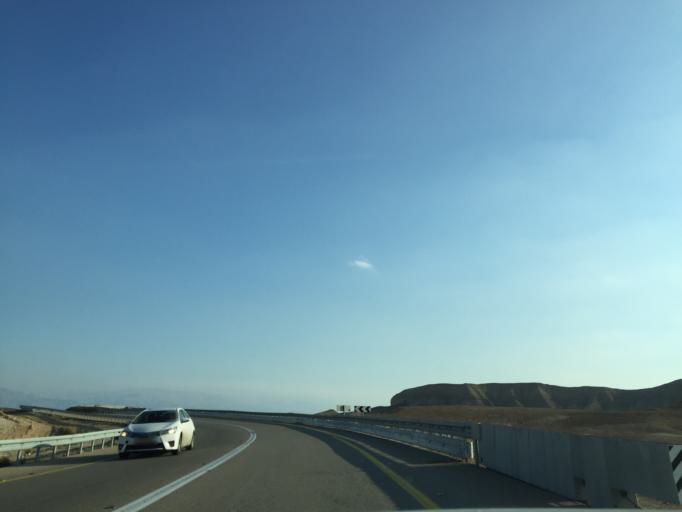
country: IL
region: Southern District
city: `En Boqeq
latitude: 31.1685
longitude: 35.3169
